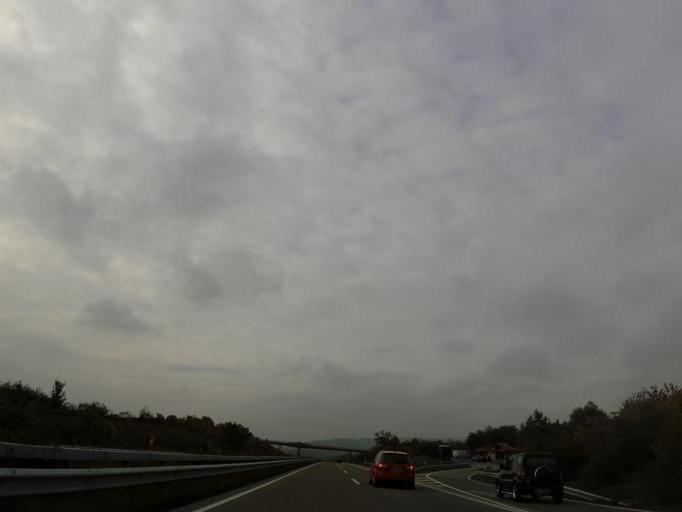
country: DE
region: Rheinland-Pfalz
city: Morschheim
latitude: 49.6875
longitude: 8.0377
